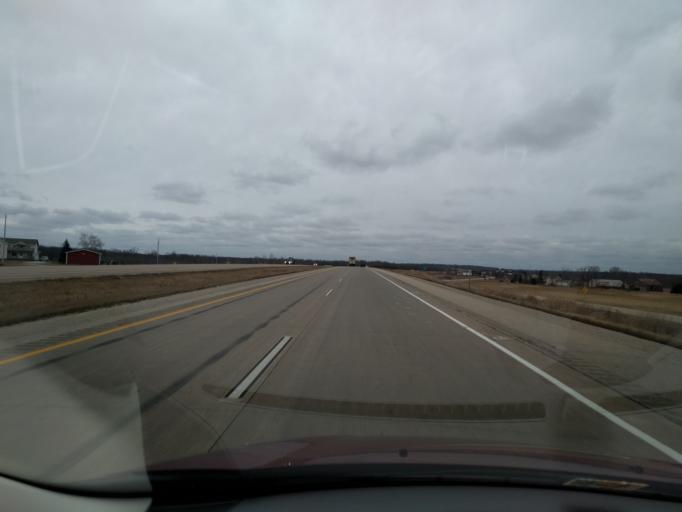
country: US
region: Wisconsin
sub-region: Winnebago County
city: Winneconne
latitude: 44.2268
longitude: -88.7108
